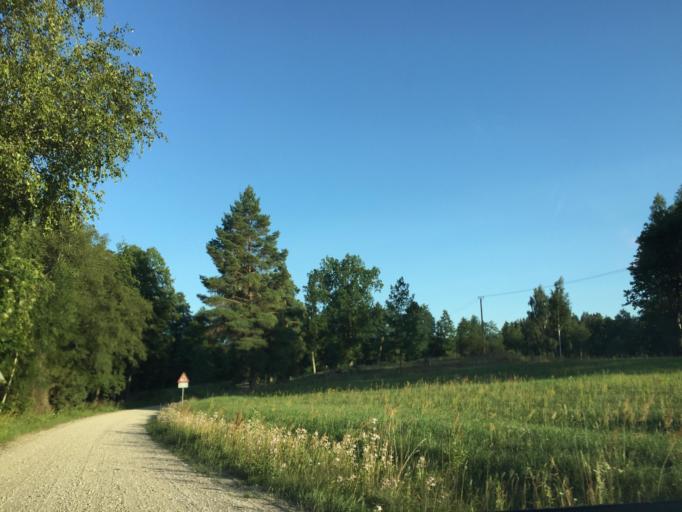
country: LV
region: Talsu Rajons
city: Stende
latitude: 57.1551
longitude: 22.2945
